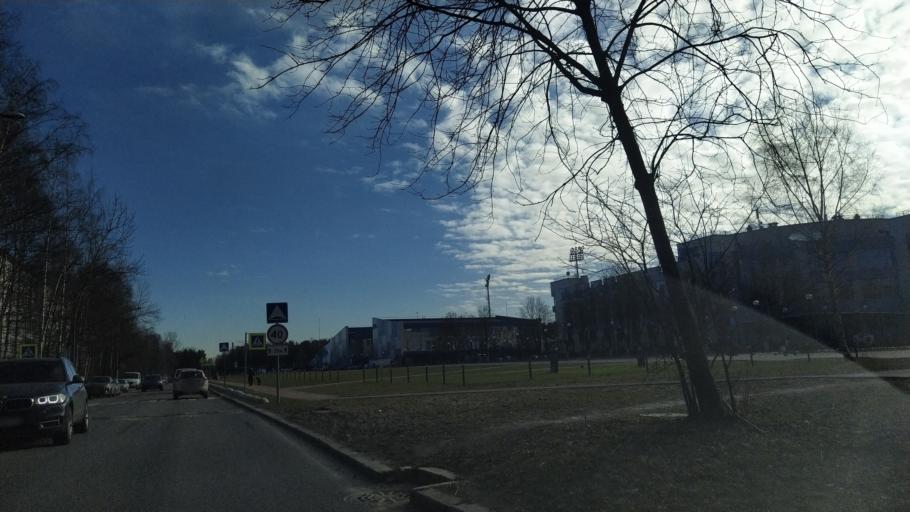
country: RU
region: Leningrad
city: Akademicheskoe
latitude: 60.0058
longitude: 30.4076
